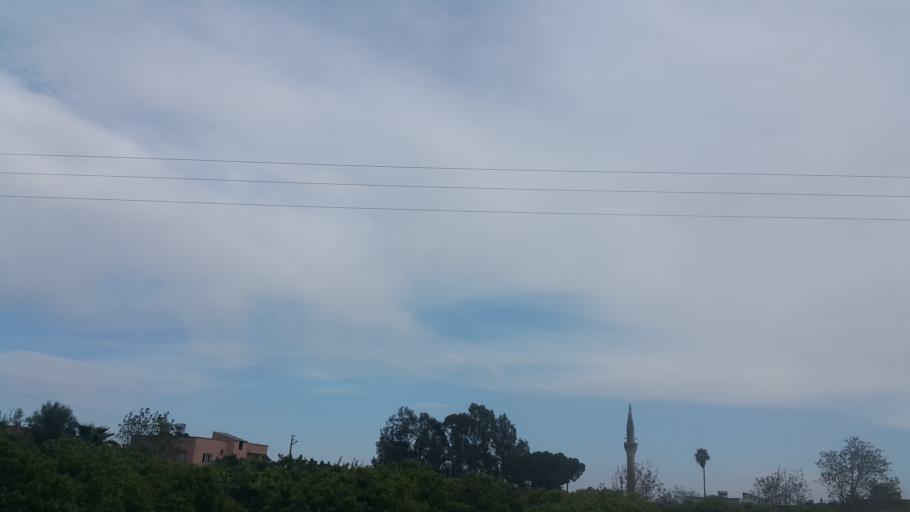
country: TR
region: Mersin
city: Tarsus
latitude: 36.9376
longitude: 34.9677
